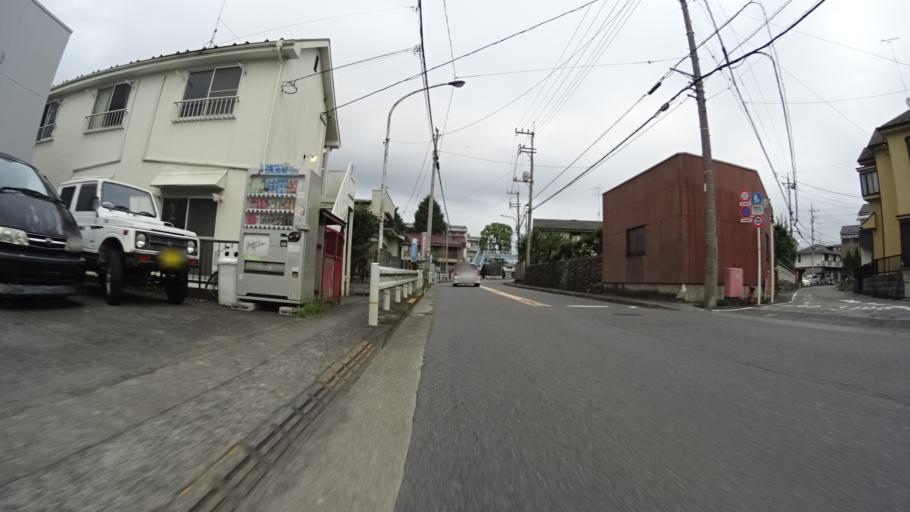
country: JP
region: Tokyo
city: Fussa
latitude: 35.7641
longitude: 139.3008
